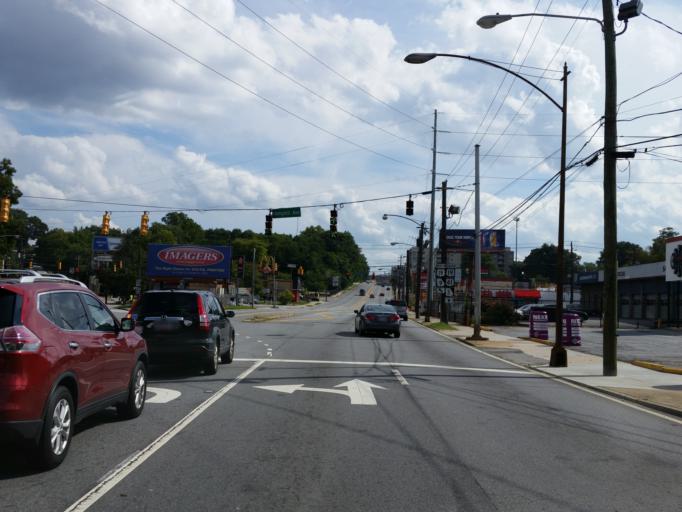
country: US
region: Georgia
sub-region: Fulton County
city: Atlanta
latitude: 33.7872
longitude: -84.4075
